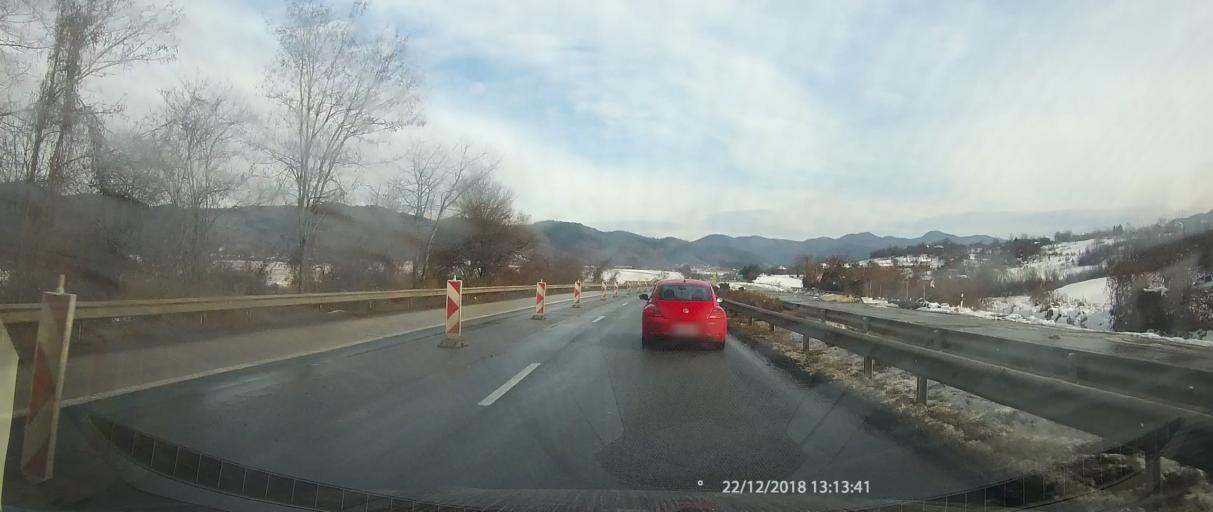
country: BG
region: Sofiya
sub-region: Obshtina Pravets
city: Pravets
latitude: 42.9067
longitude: 23.8688
